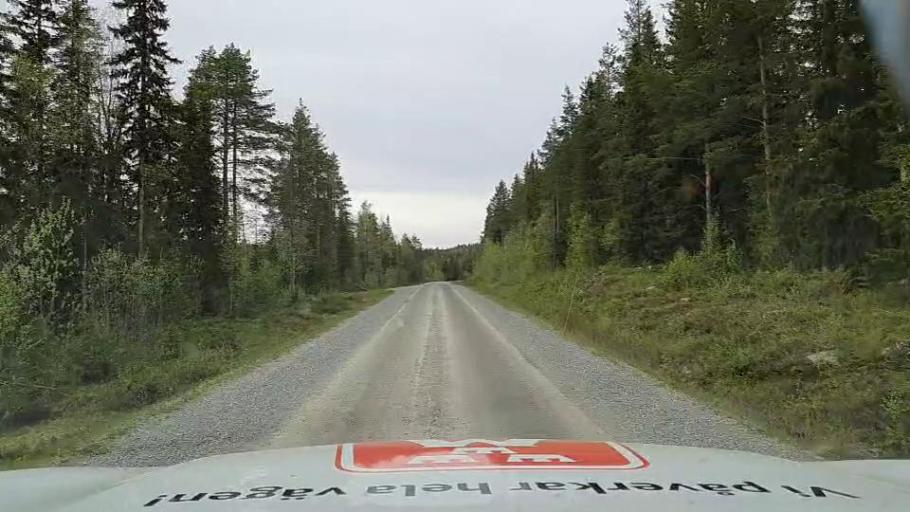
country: SE
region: Jaemtland
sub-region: OEstersunds Kommun
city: Brunflo
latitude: 62.6427
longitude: 14.9311
